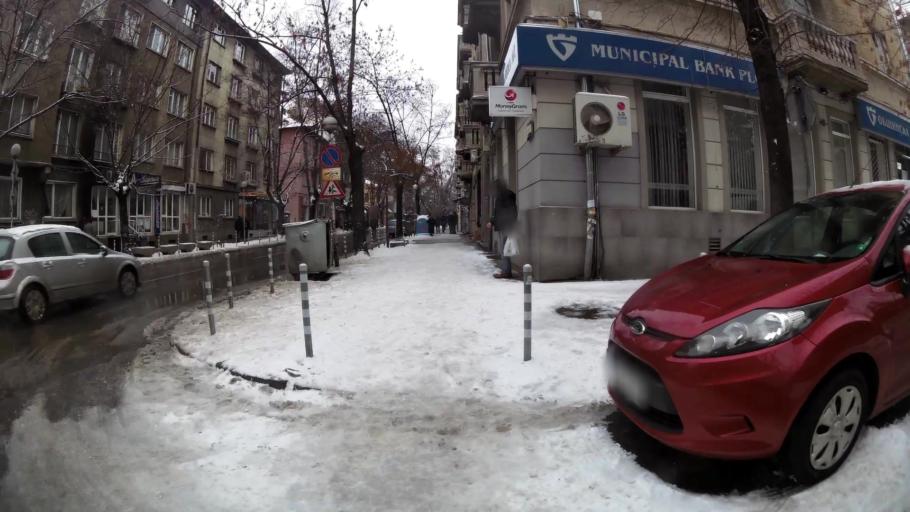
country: BG
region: Sofia-Capital
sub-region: Stolichna Obshtina
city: Sofia
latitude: 42.6936
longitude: 23.3504
